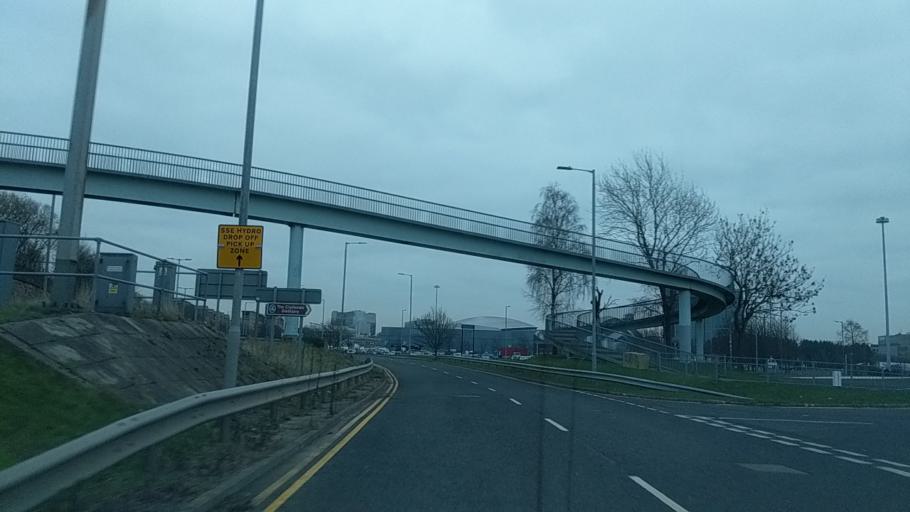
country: GB
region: Scotland
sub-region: Glasgow City
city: Glasgow
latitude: 55.8630
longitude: -4.2970
